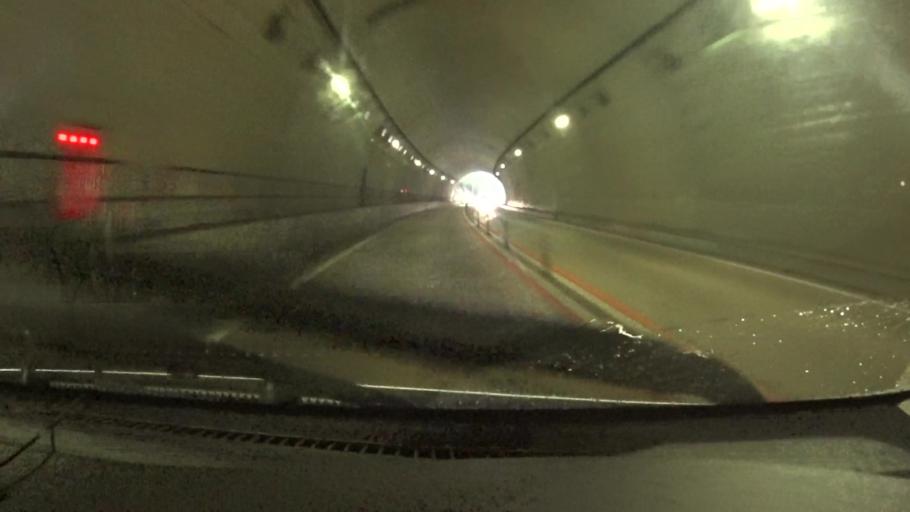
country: JP
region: Kyoto
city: Kameoka
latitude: 35.1261
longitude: 135.4763
